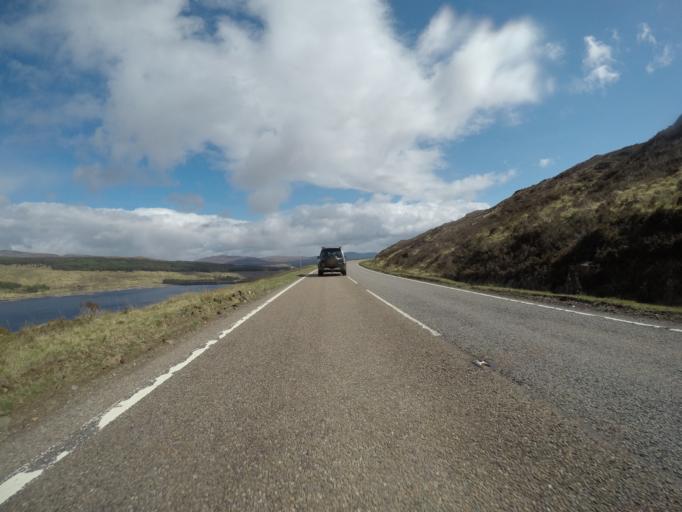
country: GB
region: Scotland
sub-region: Highland
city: Spean Bridge
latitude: 57.1189
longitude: -4.9787
